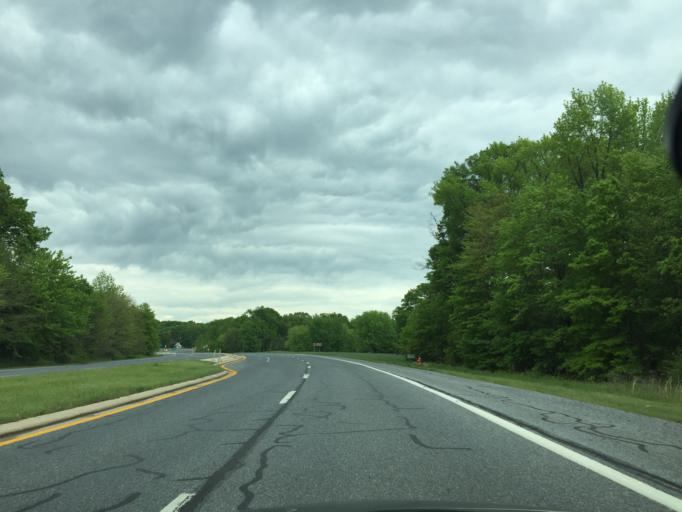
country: US
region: Maryland
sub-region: Baltimore County
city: Middle River
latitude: 39.2940
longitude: -76.4342
